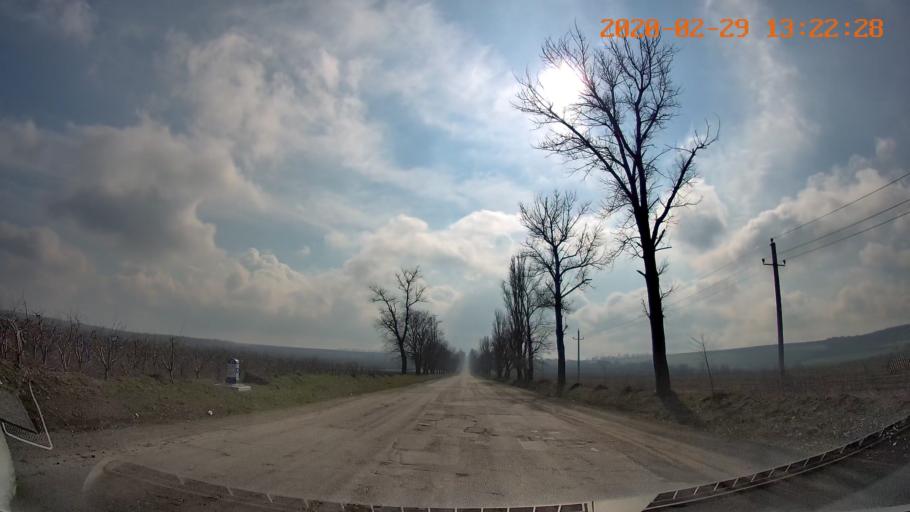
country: MD
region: Telenesti
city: Camenca
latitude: 47.9601
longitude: 28.6278
